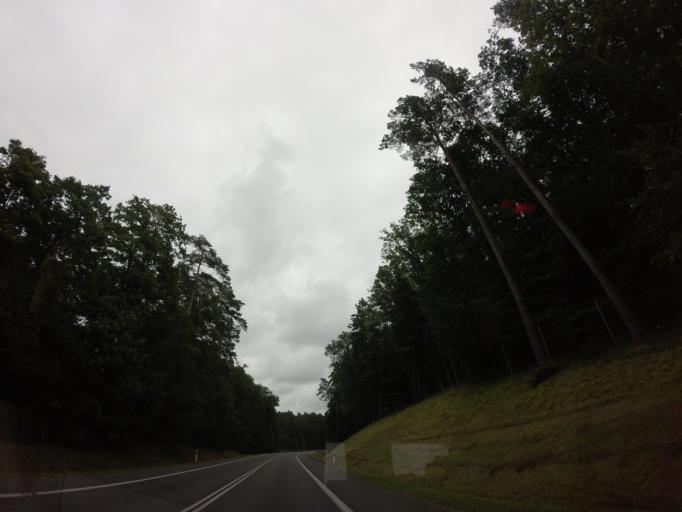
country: PL
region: West Pomeranian Voivodeship
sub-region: Powiat kamienski
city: Miedzyzdroje
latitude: 53.8965
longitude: 14.4737
